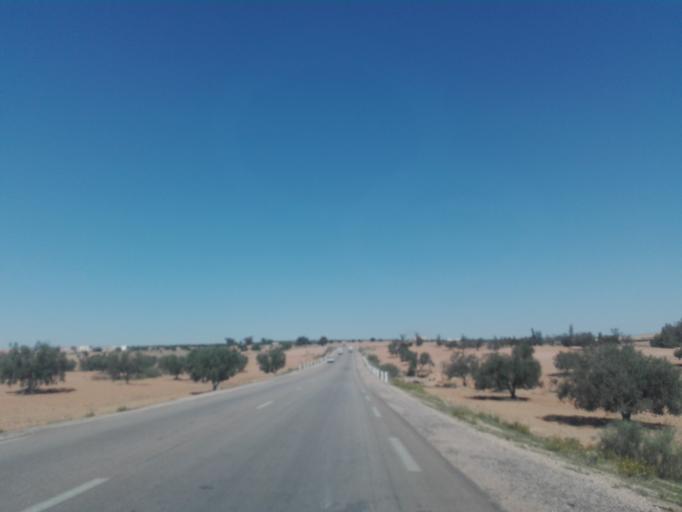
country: TN
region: Safaqis
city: Bi'r `Ali Bin Khalifah
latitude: 34.7444
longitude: 10.3641
